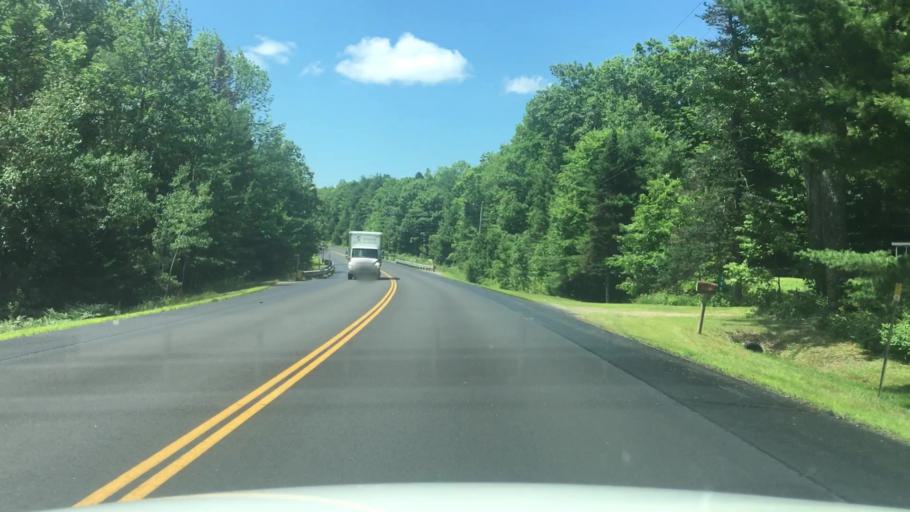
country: US
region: Maine
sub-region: Waldo County
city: Searsmont
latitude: 44.4096
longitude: -69.1889
